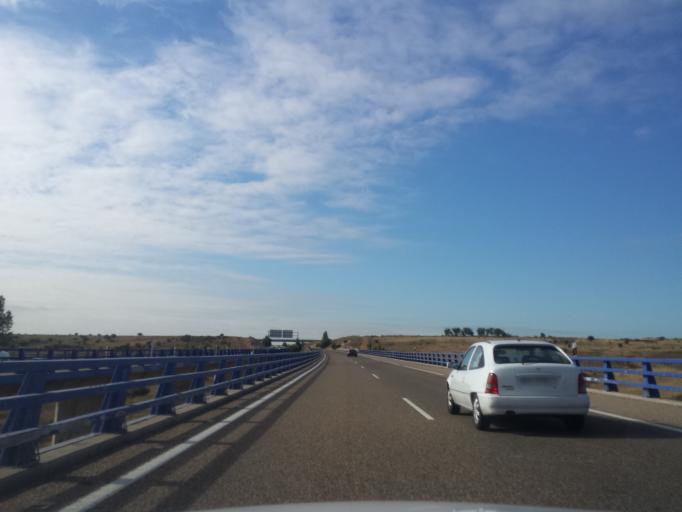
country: ES
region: Castille and Leon
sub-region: Provincia de Leon
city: Onzonilla
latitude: 42.4922
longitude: -5.6001
